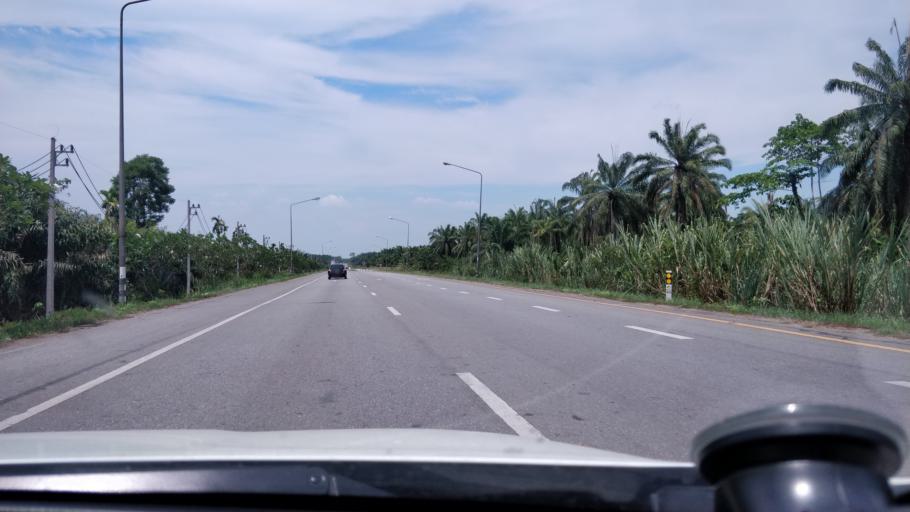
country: TH
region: Krabi
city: Plai Phraya
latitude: 8.6190
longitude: 98.9982
